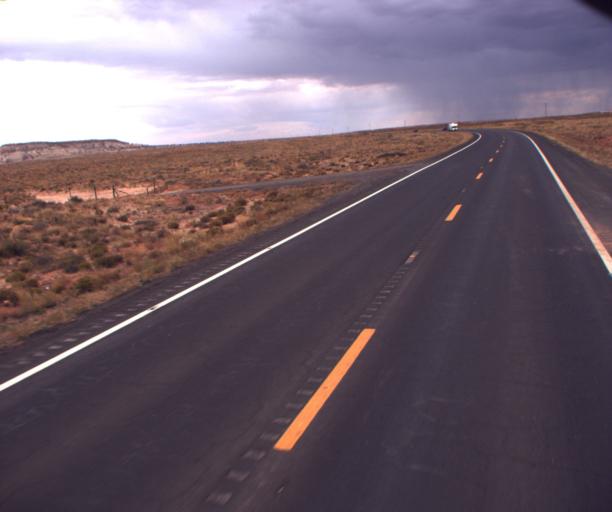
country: US
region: Arizona
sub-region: Coconino County
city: Tuba City
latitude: 36.2722
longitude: -111.0136
